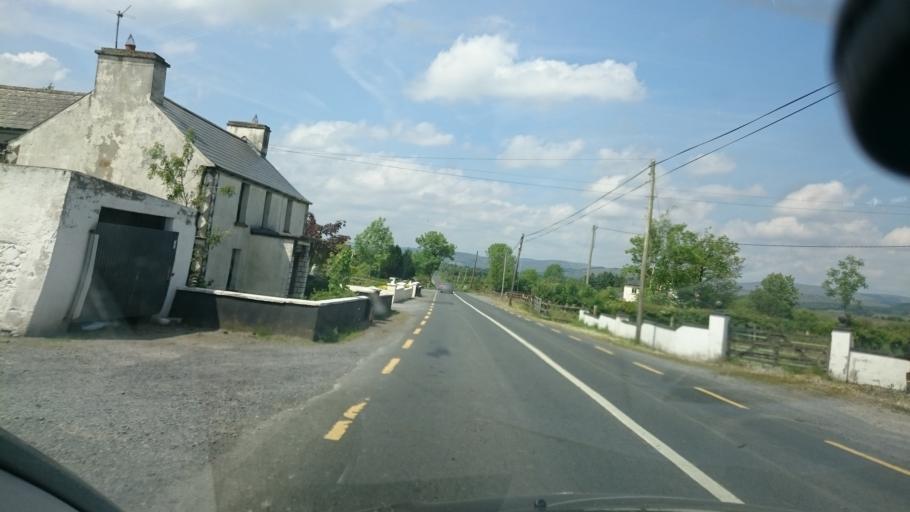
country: IE
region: Connaught
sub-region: Sligo
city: Tobercurry
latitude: 54.0568
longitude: -8.8008
